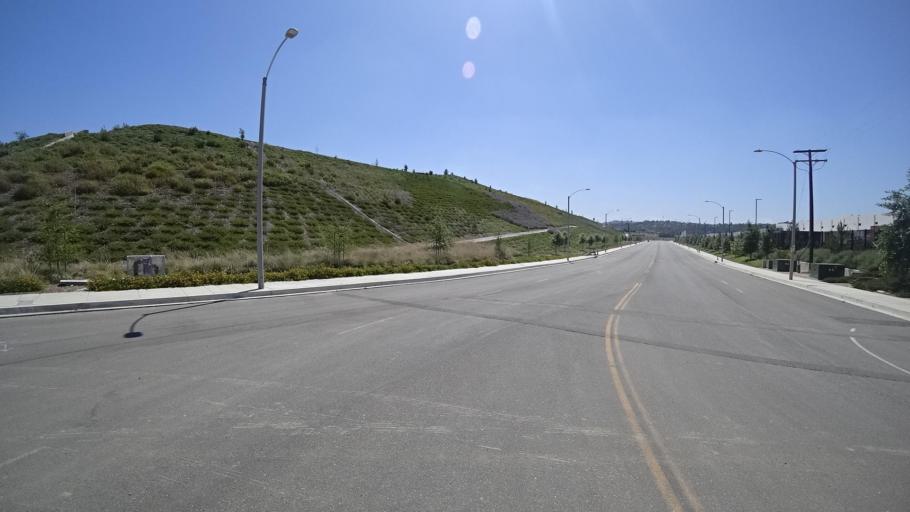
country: US
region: California
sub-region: Los Angeles County
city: Diamond Bar
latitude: 34.0218
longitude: -117.8234
